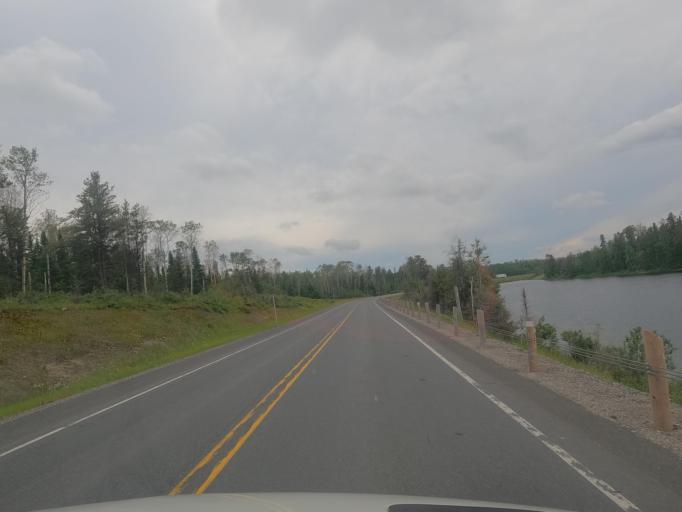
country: CA
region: Ontario
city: Greenstone
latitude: 49.6783
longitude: -87.5604
